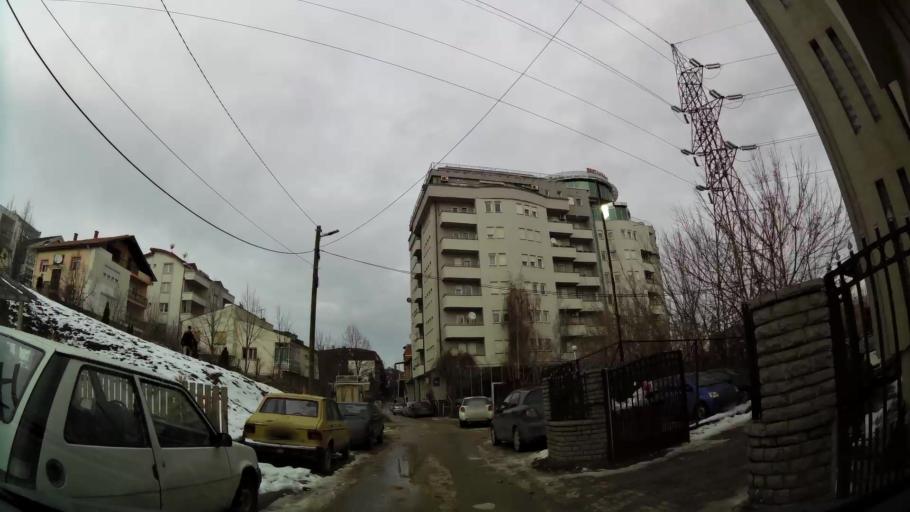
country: XK
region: Pristina
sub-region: Komuna e Prishtines
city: Pristina
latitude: 42.6650
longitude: 21.1546
